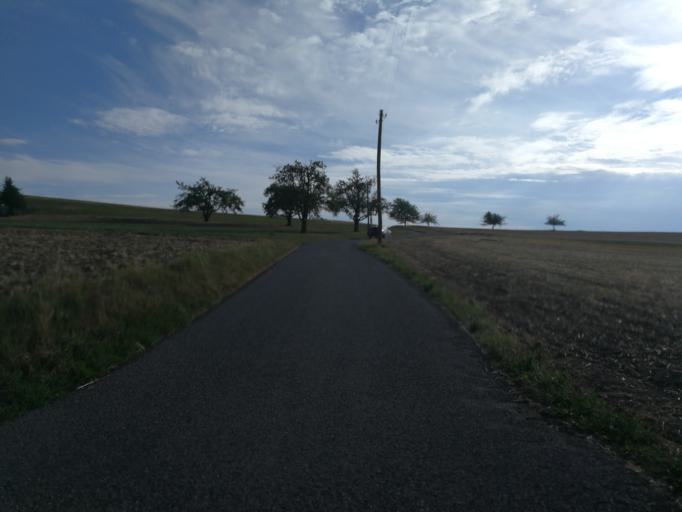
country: CH
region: Zurich
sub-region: Bezirk Meilen
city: Oetwil am See
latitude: 47.2717
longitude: 8.7358
